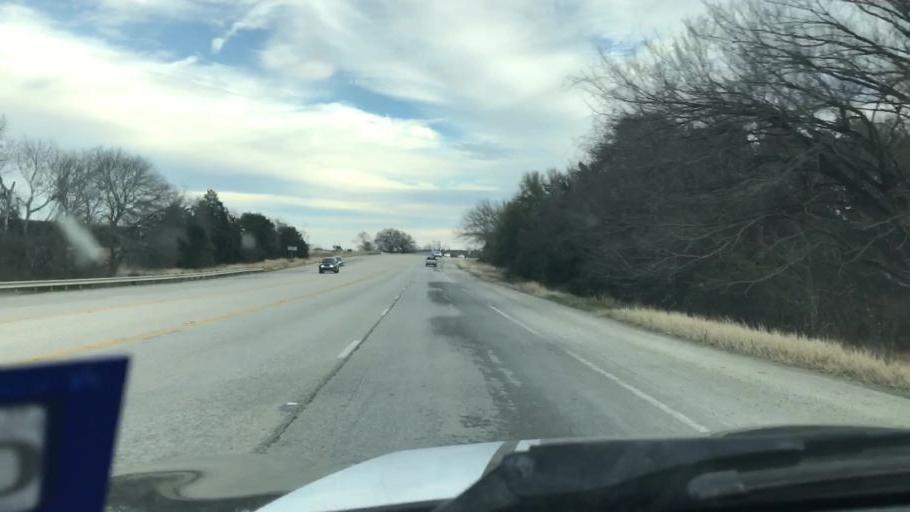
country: US
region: Texas
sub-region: Bastrop County
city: Camp Swift
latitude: 30.2875
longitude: -97.2486
